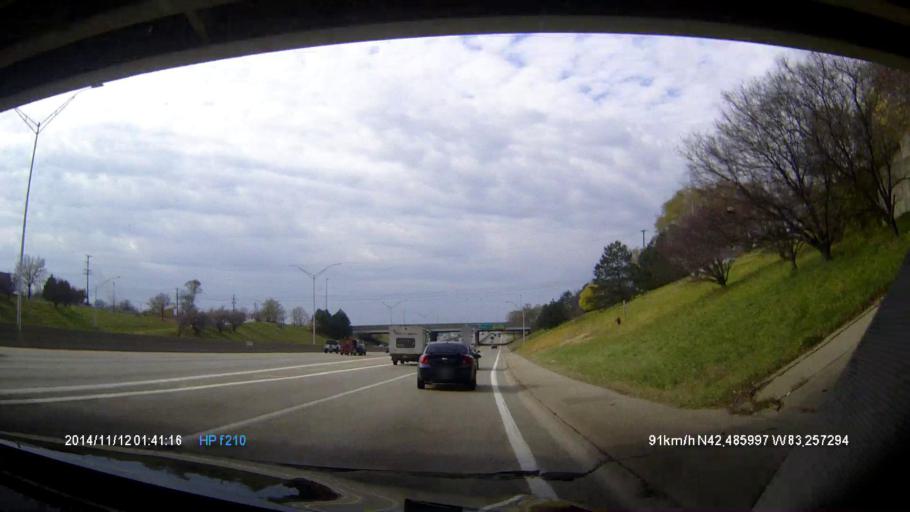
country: US
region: Michigan
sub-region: Oakland County
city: Bingham Farms
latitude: 42.4861
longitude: -83.2574
